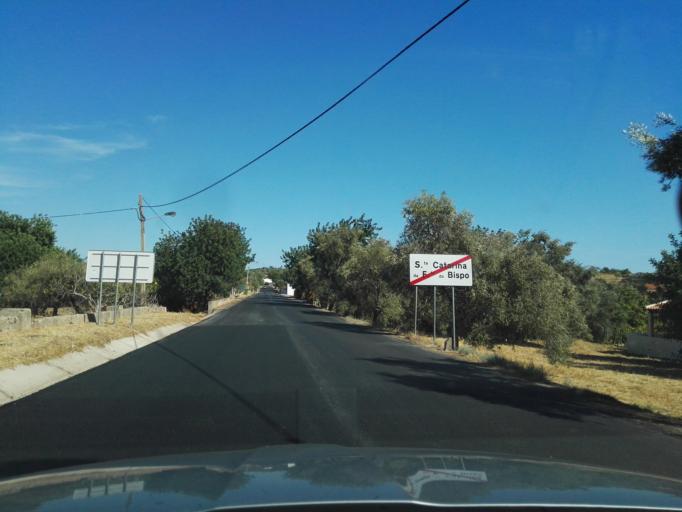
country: PT
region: Faro
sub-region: Olhao
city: Moncarapacho
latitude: 37.1533
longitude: -7.7837
